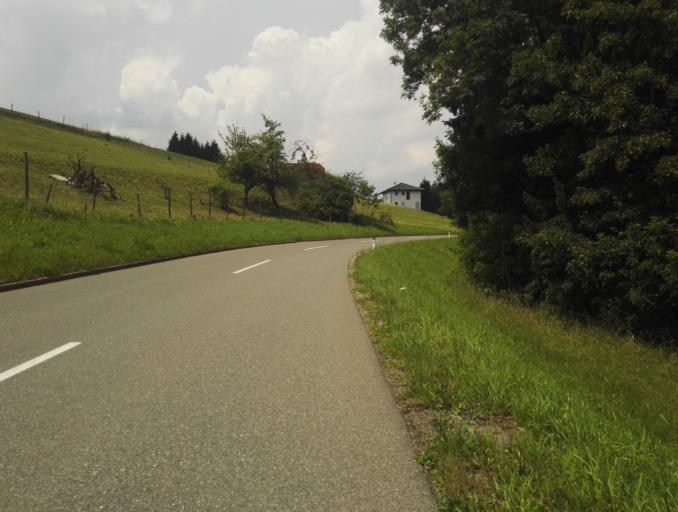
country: AT
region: Styria
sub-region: Politischer Bezirk Graz-Umgebung
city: Sankt Oswald bei Plankenwarth
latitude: 47.0870
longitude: 15.2933
